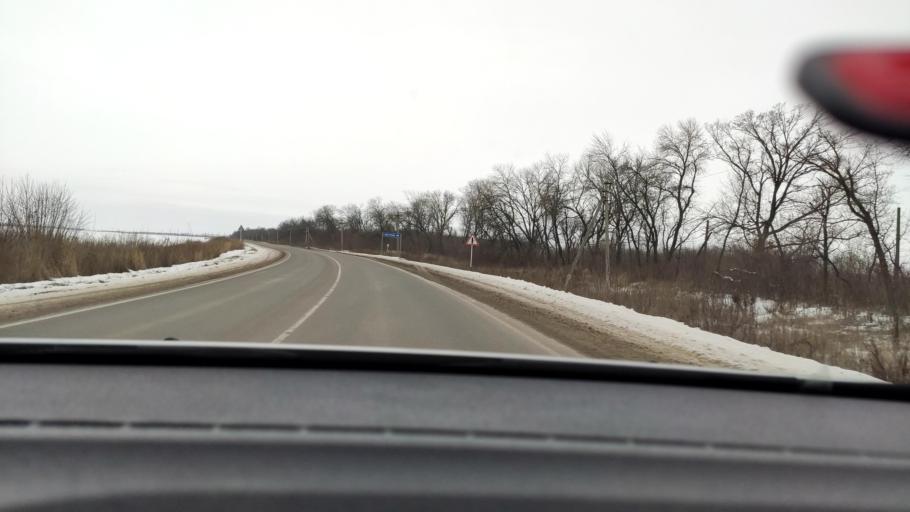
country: RU
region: Voronezj
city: Semiluki
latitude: 51.7284
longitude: 38.9852
